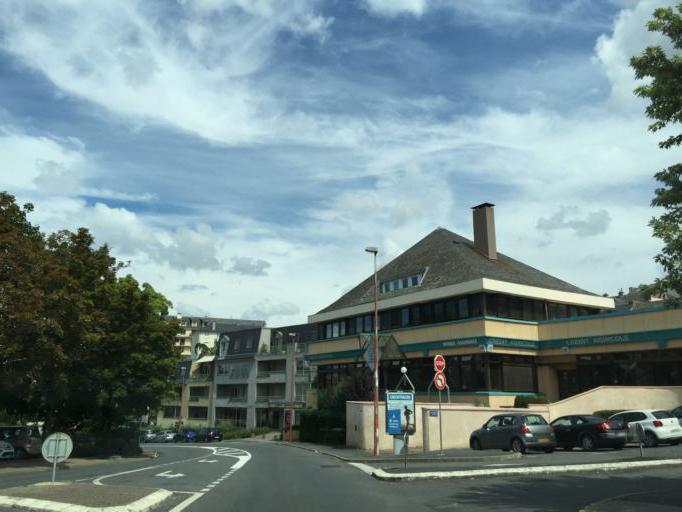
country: FR
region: Midi-Pyrenees
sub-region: Departement de l'Aveyron
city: Rodez
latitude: 44.3530
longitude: 2.5688
